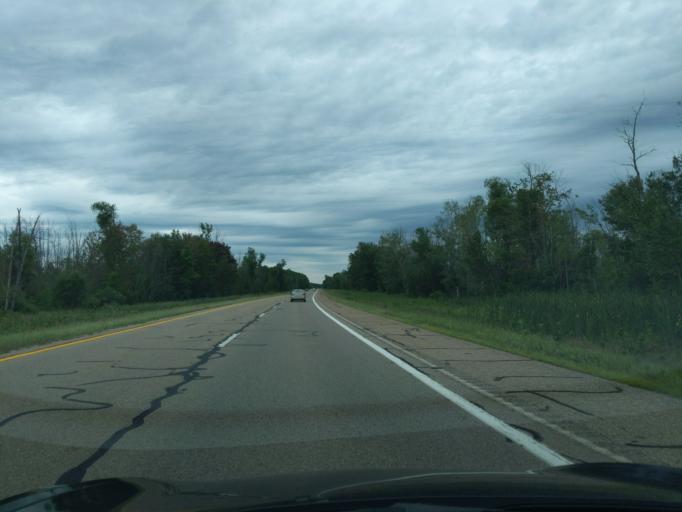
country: US
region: Michigan
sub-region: Roscommon County
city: Houghton Lake
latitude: 44.2975
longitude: -84.8015
